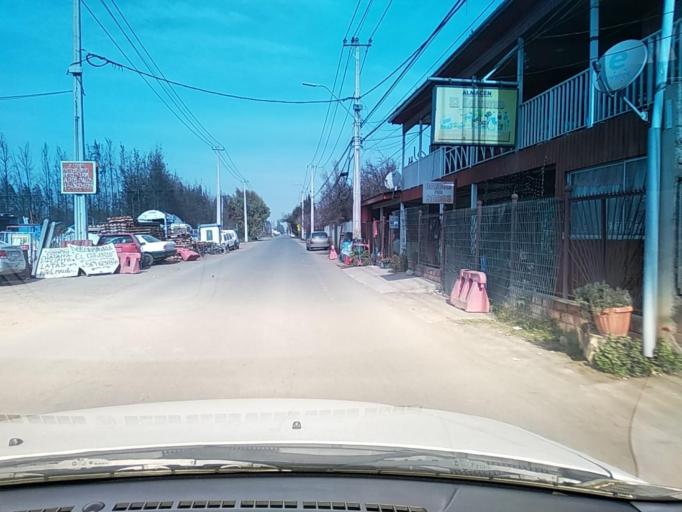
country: CL
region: Santiago Metropolitan
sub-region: Provincia de Chacabuco
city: Chicureo Abajo
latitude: -33.2857
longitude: -70.7298
